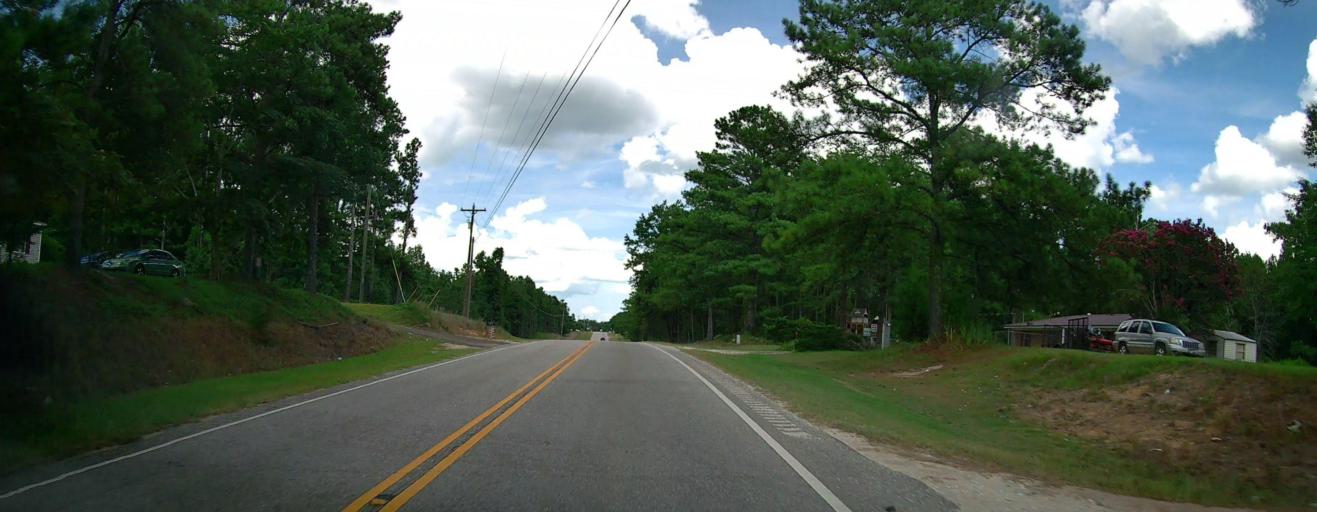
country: US
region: Alabama
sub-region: Macon County
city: Tuskegee
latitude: 32.4623
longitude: -85.6059
